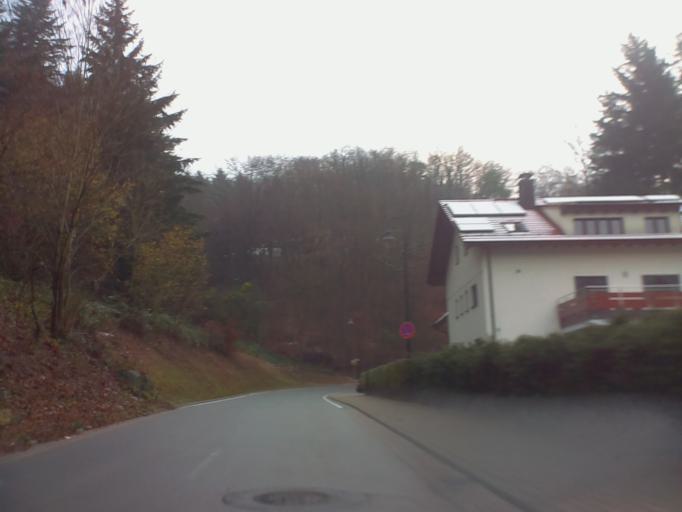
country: DE
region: Baden-Wuerttemberg
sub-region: Karlsruhe Region
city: Weinheim
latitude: 49.5106
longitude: 8.6915
